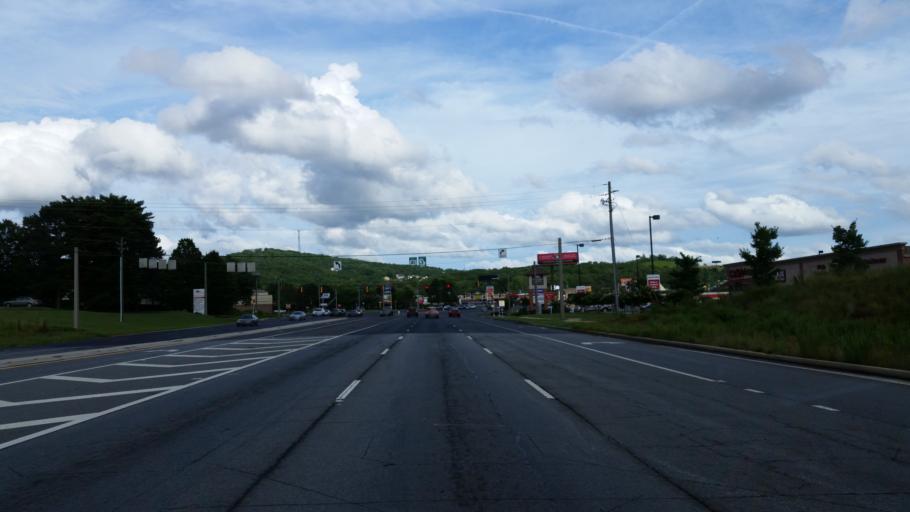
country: US
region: Georgia
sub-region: Bartow County
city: Cartersville
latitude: 34.1996
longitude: -84.7955
